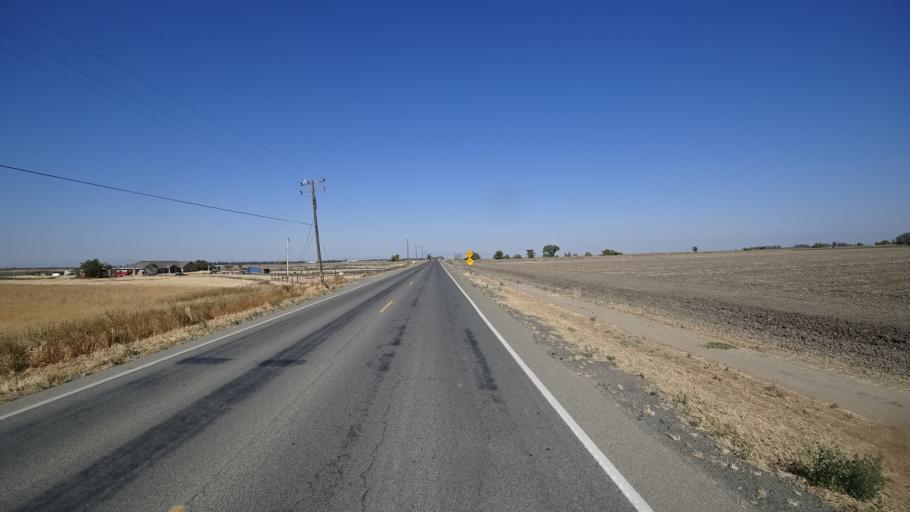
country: US
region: California
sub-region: Kings County
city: Lemoore Station
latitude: 36.3437
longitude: -119.8913
